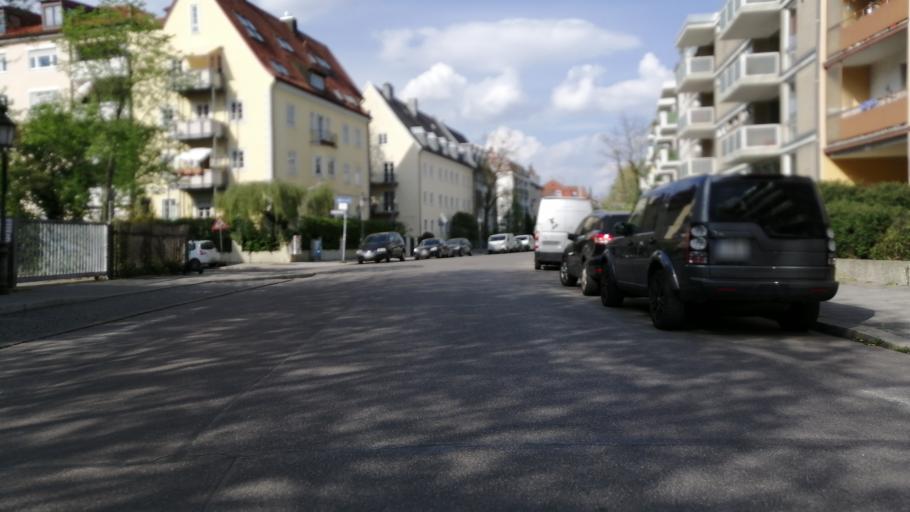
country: DE
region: Bavaria
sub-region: Upper Bavaria
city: Bogenhausen
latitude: 48.1642
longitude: 11.5903
